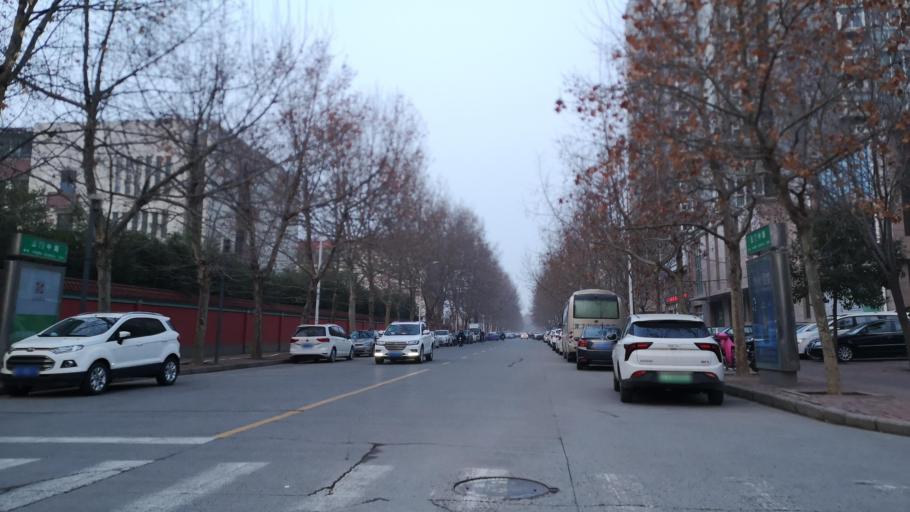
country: CN
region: Henan Sheng
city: Zhongyuanlu
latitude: 35.7534
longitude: 115.0607
